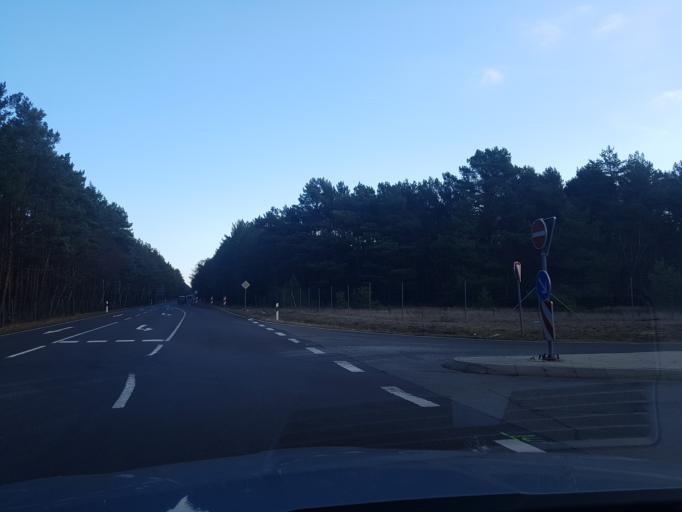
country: DE
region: Brandenburg
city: Kasel-Golzig
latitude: 52.0170
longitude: 13.7003
